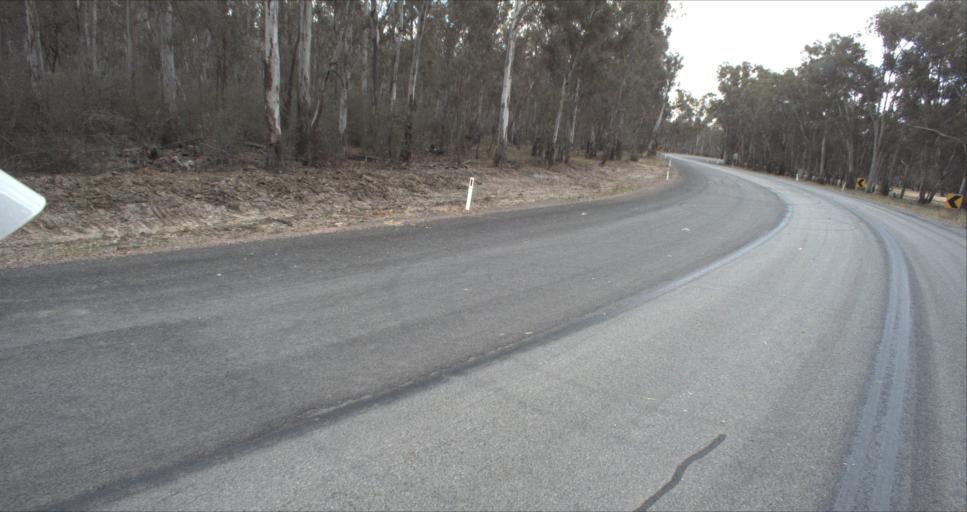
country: AU
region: New South Wales
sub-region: Leeton
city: Leeton
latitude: -34.6337
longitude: 146.3756
